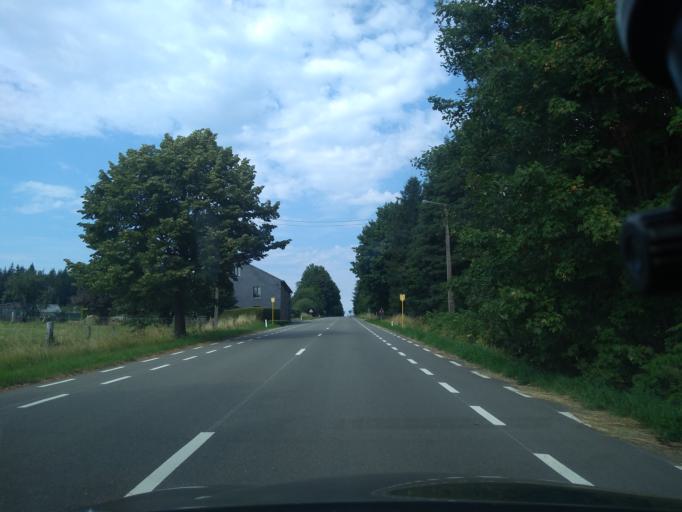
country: BE
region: Wallonia
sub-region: Province du Luxembourg
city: Libin
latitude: 49.9936
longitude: 5.2668
